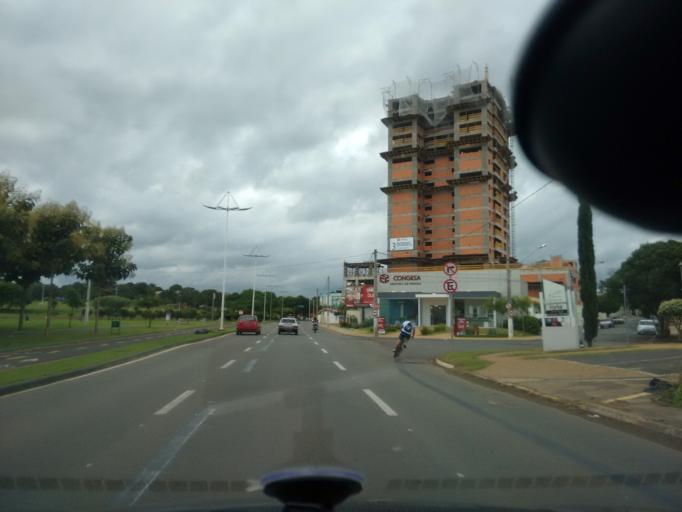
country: BR
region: Sao Paulo
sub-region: Indaiatuba
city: Indaiatuba
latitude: -23.0835
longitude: -47.2232
